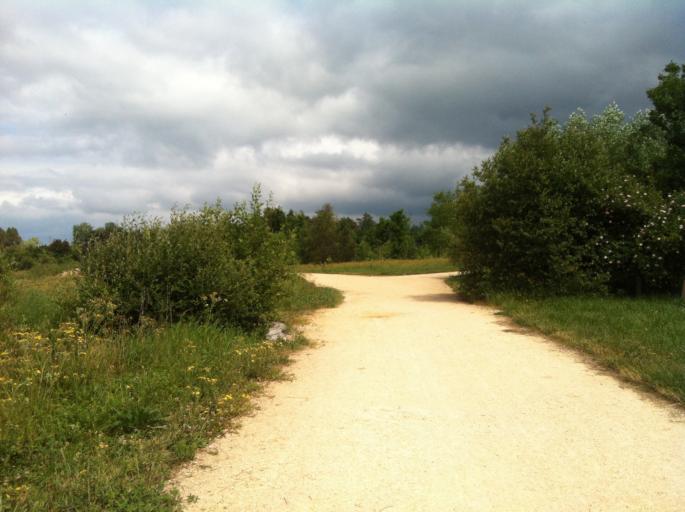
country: ES
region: Basque Country
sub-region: Provincia de Alava
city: Gasteiz / Vitoria
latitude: 42.8300
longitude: -2.6643
